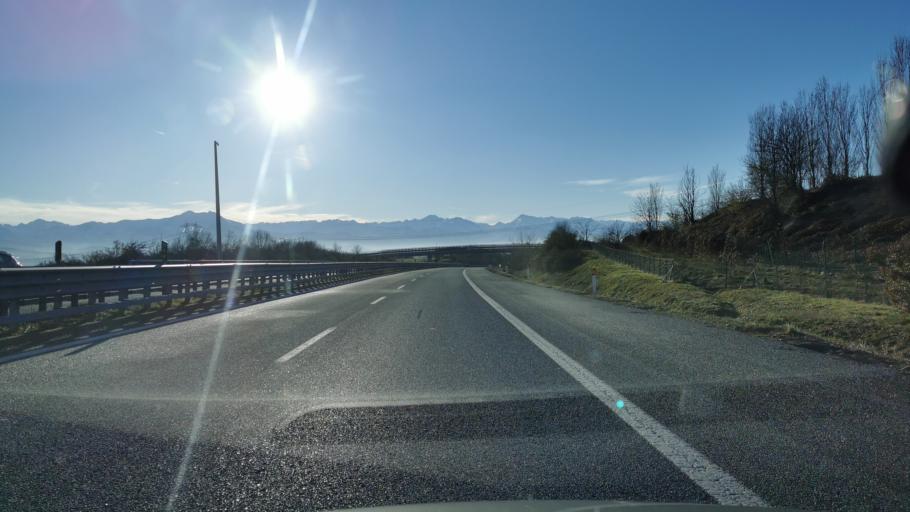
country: IT
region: Piedmont
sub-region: Provincia di Cuneo
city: Magliano Alpi
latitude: 44.4726
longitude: 7.7865
